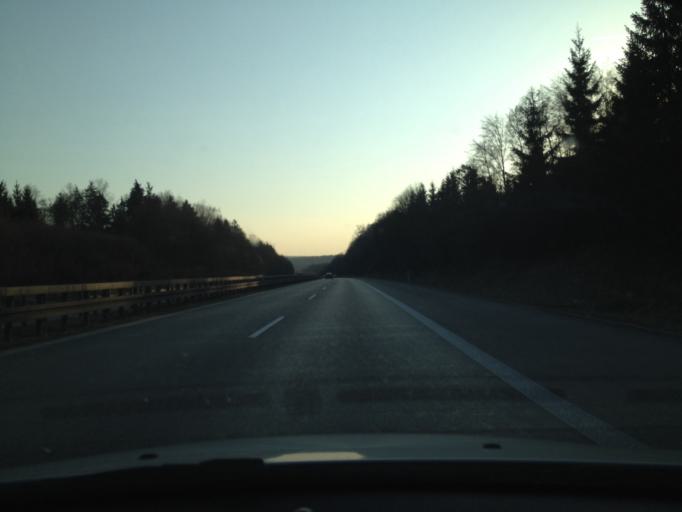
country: DE
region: Baden-Wuerttemberg
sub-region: Tuebingen Region
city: Setzingen
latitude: 48.5517
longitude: 10.1127
